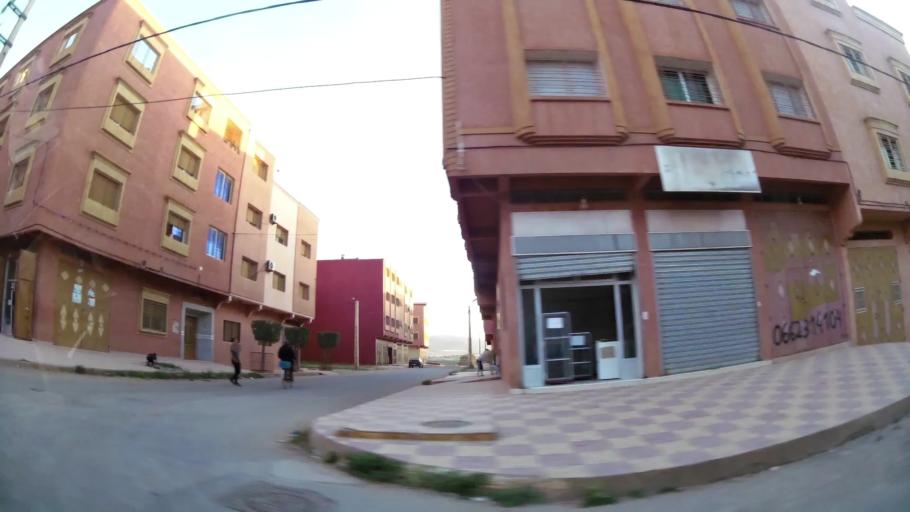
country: MA
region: Oriental
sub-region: Berkane-Taourirt
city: Berkane
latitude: 34.9167
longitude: -2.3238
